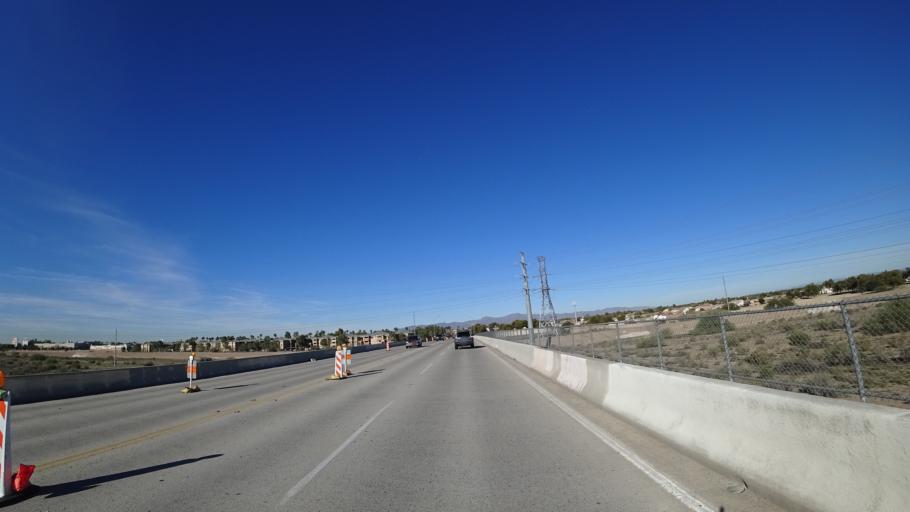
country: US
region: Arizona
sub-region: Maricopa County
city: Avondale
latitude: 33.4626
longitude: -112.3301
